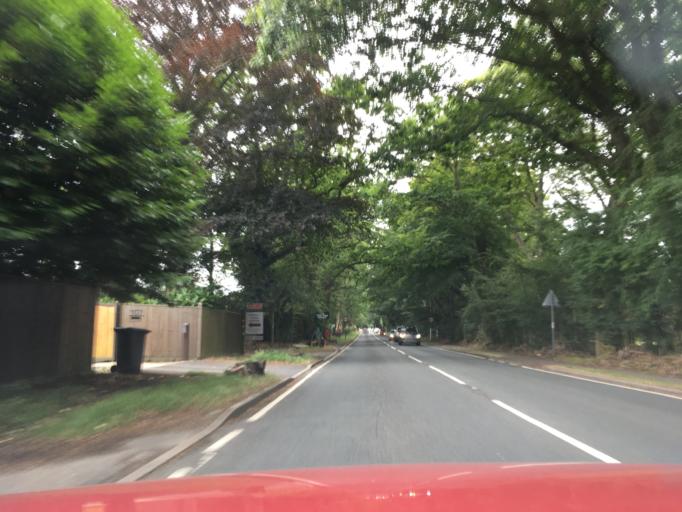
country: GB
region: England
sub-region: Surrey
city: Felbridge
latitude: 51.1430
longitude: -0.0600
